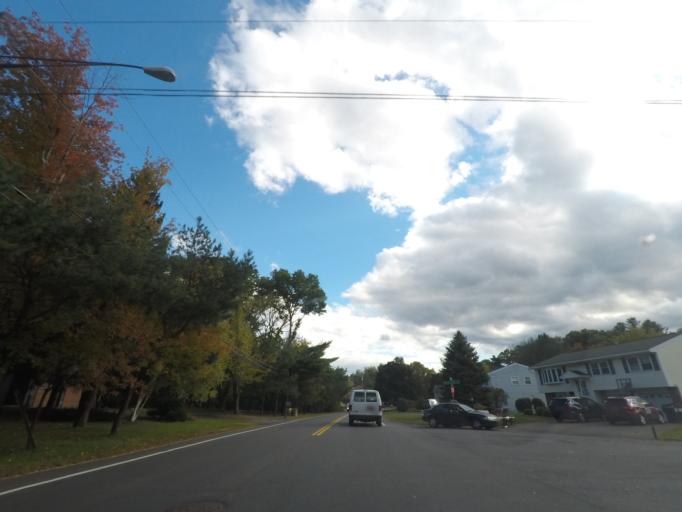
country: US
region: New York
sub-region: Albany County
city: Colonie
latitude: 42.7486
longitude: -73.8379
